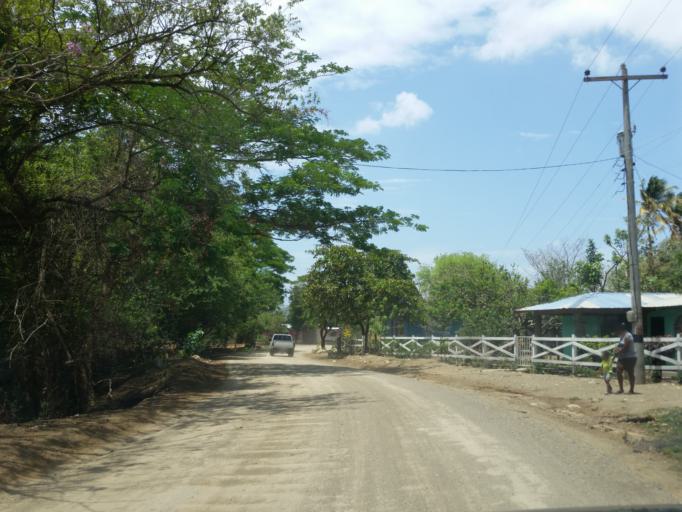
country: NI
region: Rivas
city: Tola
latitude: 11.4538
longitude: -86.0686
